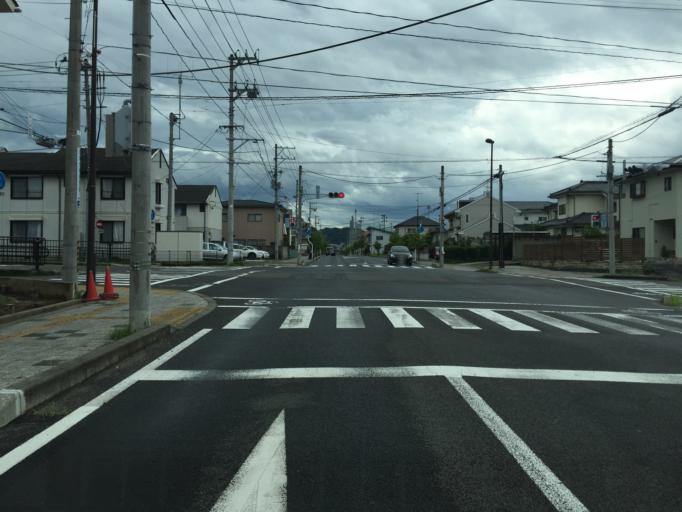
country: JP
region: Fukushima
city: Fukushima-shi
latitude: 37.7605
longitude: 140.4844
